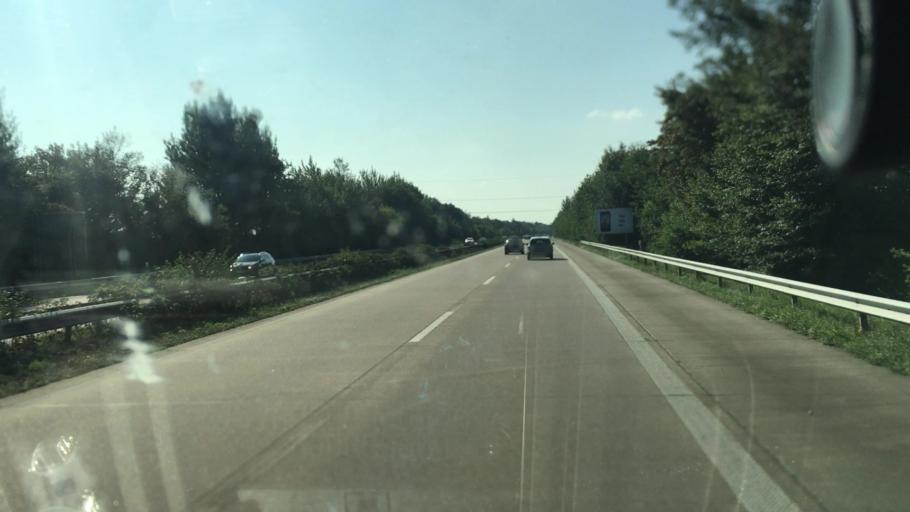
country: DE
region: Lower Saxony
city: Wiefelstede
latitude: 53.3159
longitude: 8.1405
